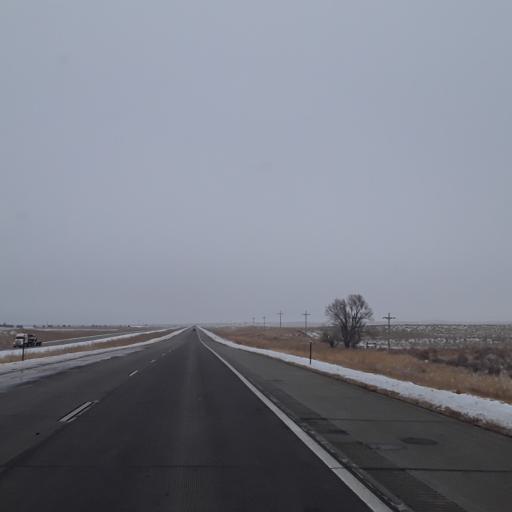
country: US
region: Colorado
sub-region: Logan County
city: Sterling
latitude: 40.5234
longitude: -103.2391
